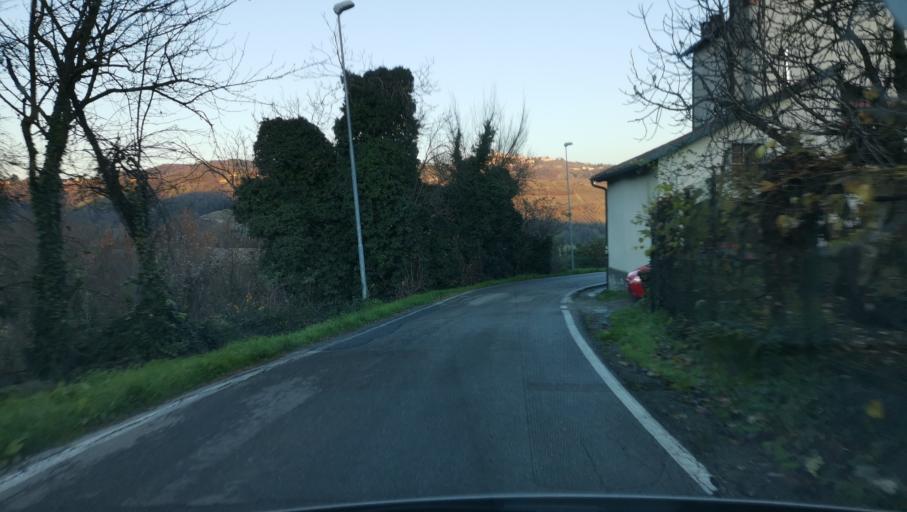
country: IT
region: Piedmont
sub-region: Provincia di Asti
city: Moncucco Torinese
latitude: 45.0646
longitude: 7.9382
